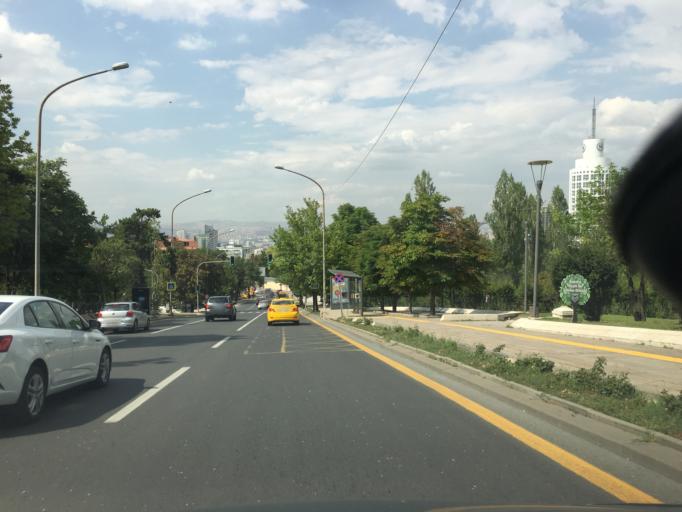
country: TR
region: Ankara
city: Cankaya
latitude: 39.8951
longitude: 32.8621
